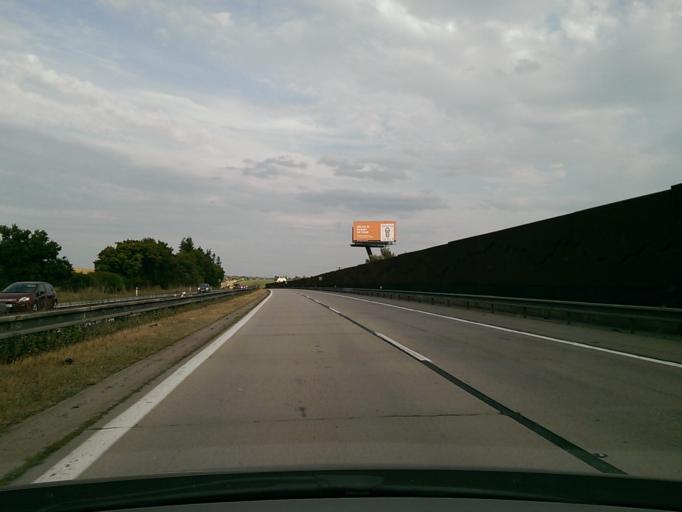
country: CZ
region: Vysocina
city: Merin
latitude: 49.3923
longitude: 15.8988
